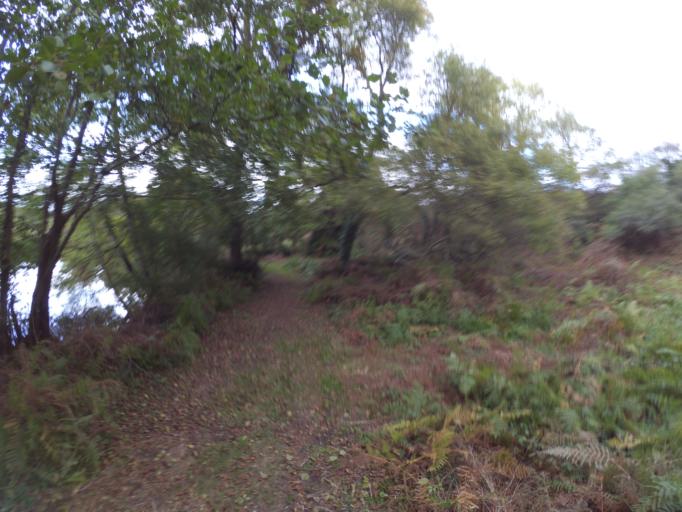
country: FR
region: Pays de la Loire
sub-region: Departement de la Loire-Atlantique
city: Remouille
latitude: 47.0644
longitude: -1.3752
